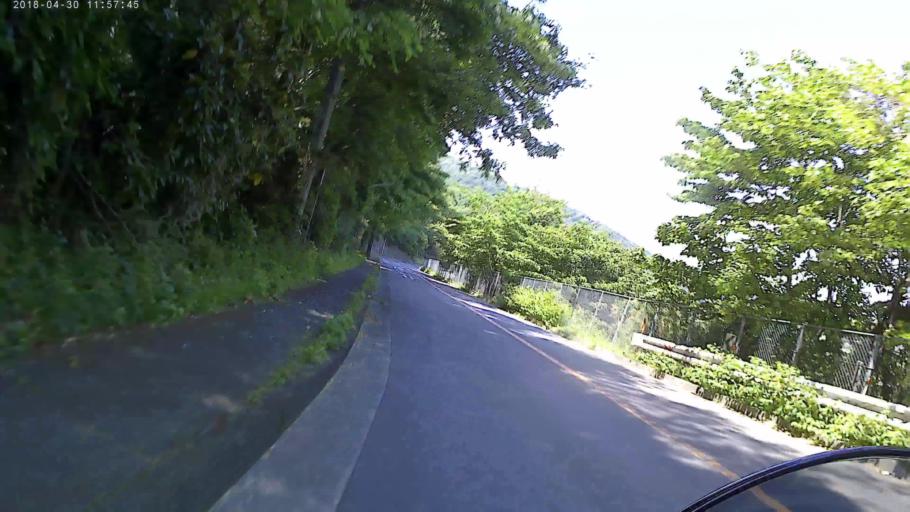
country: JP
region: Kanagawa
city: Zama
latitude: 35.4978
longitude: 139.3412
